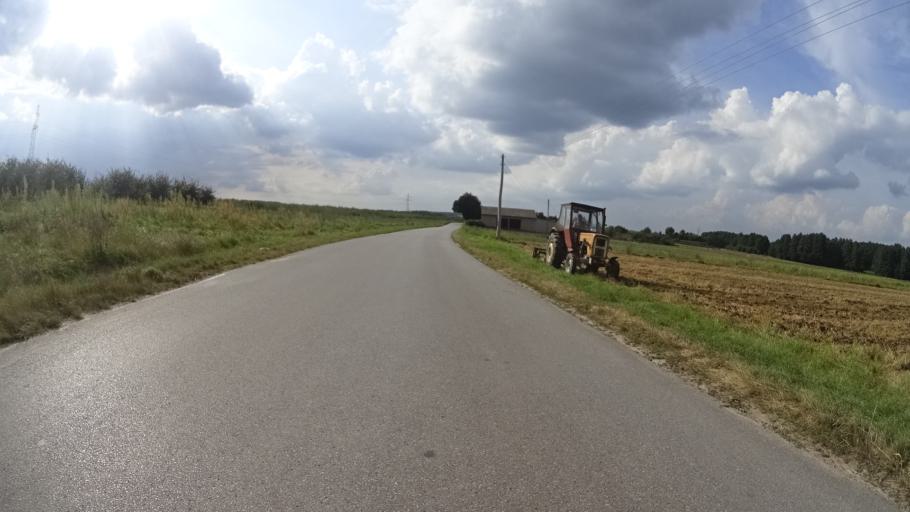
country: PL
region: Masovian Voivodeship
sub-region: Powiat grojecki
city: Mogielnica
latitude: 51.6593
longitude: 20.7497
